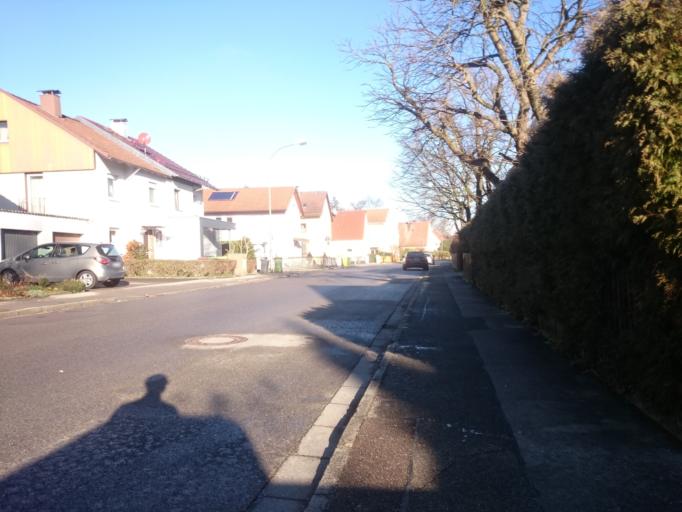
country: DE
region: Bavaria
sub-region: Swabia
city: Konigsbrunn
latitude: 48.3015
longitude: 10.9064
